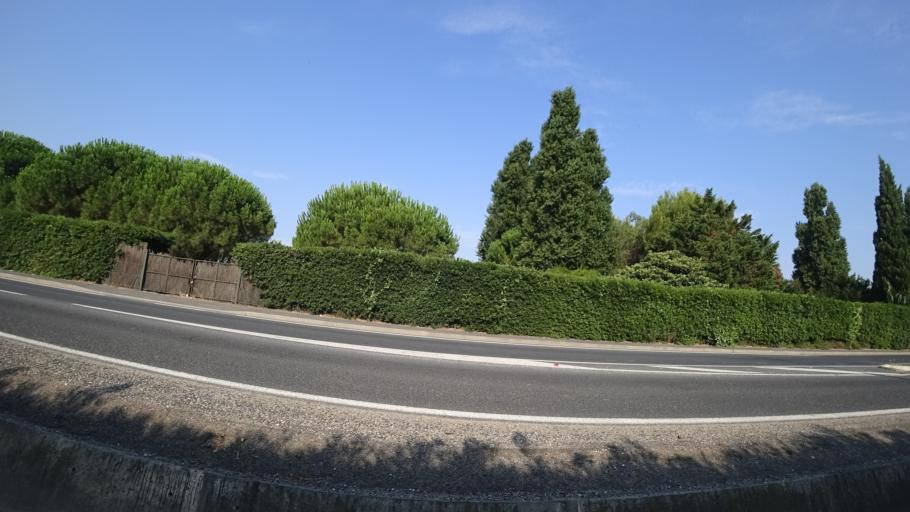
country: FR
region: Languedoc-Roussillon
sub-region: Departement des Pyrenees-Orientales
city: Bompas
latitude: 42.7206
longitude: 2.9323
